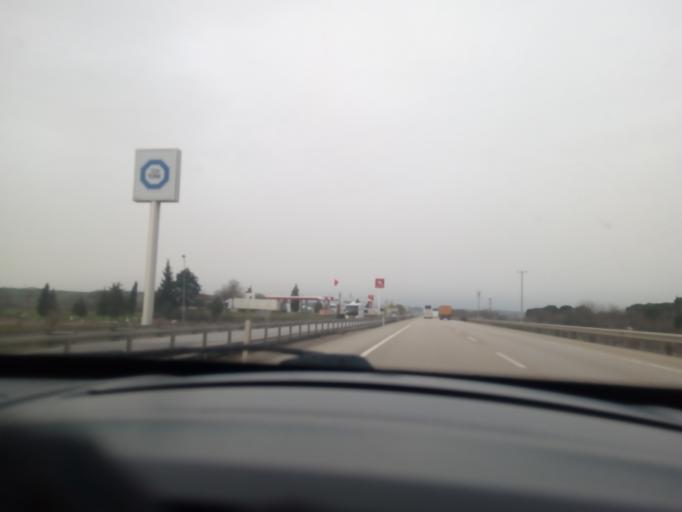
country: TR
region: Bursa
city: Tatkavakli
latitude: 40.0311
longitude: 28.3393
